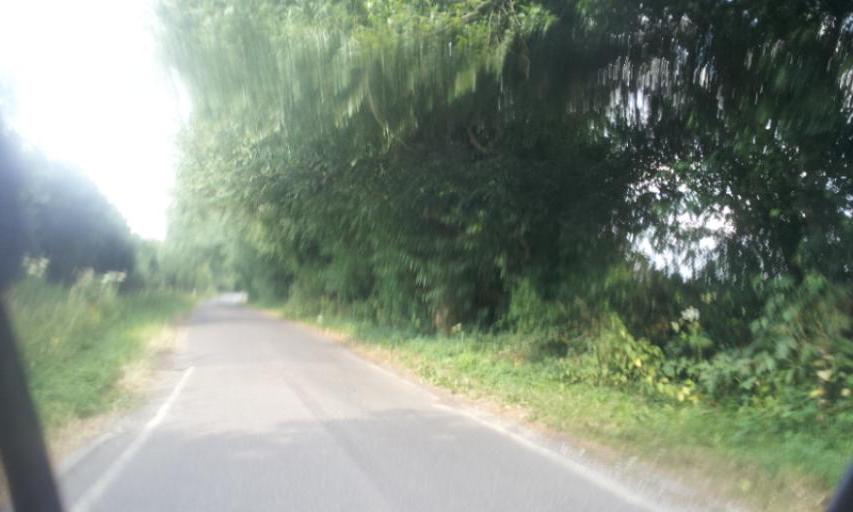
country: GB
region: England
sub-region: Kent
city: Yalding
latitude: 51.1958
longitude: 0.4243
